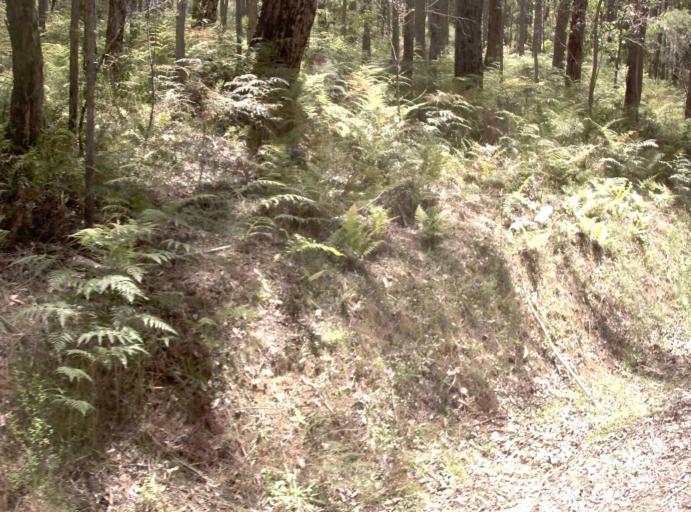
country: AU
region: New South Wales
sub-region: Bombala
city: Bombala
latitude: -37.4855
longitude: 148.9301
